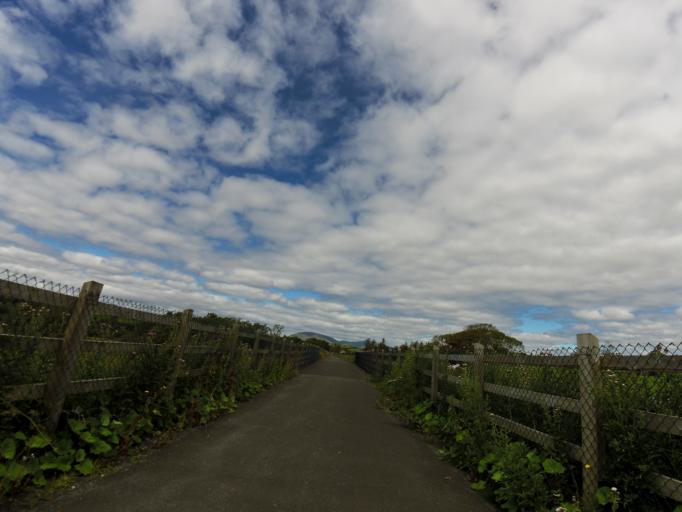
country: IE
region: Connaught
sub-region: Maigh Eo
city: Westport
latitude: 53.8435
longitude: -9.5513
